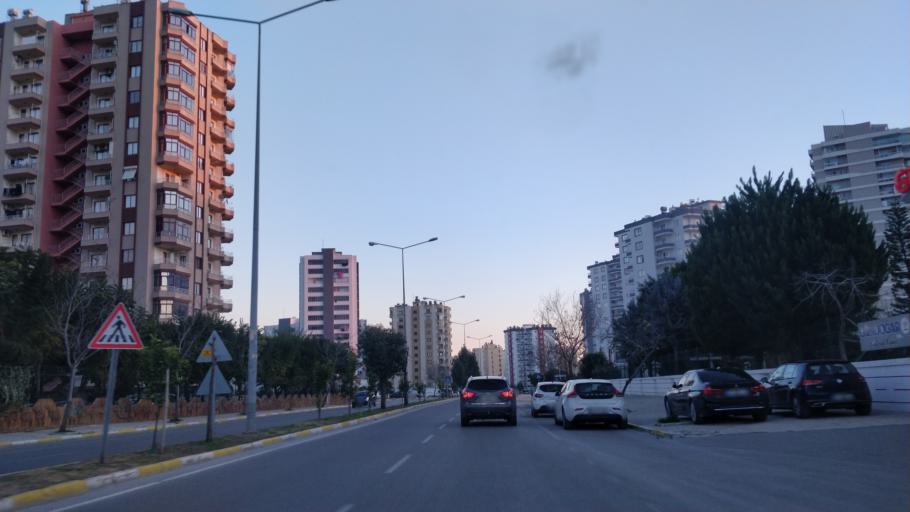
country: TR
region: Mersin
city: Mercin
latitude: 36.7953
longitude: 34.5867
